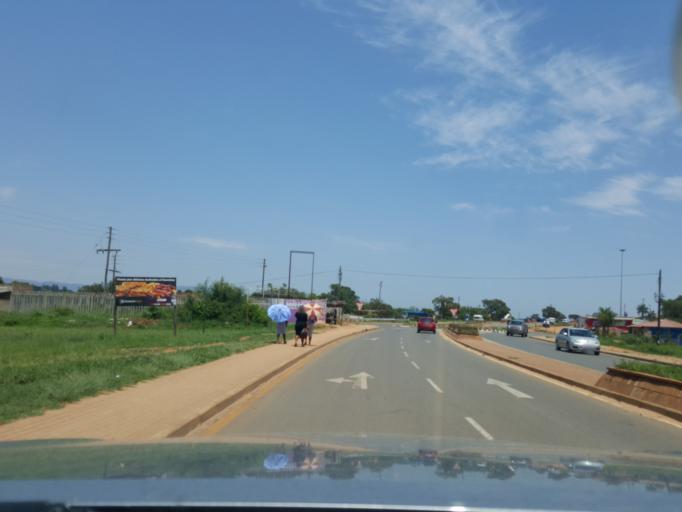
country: ZA
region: Limpopo
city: Thulamahashi
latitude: -24.8425
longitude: 31.0798
